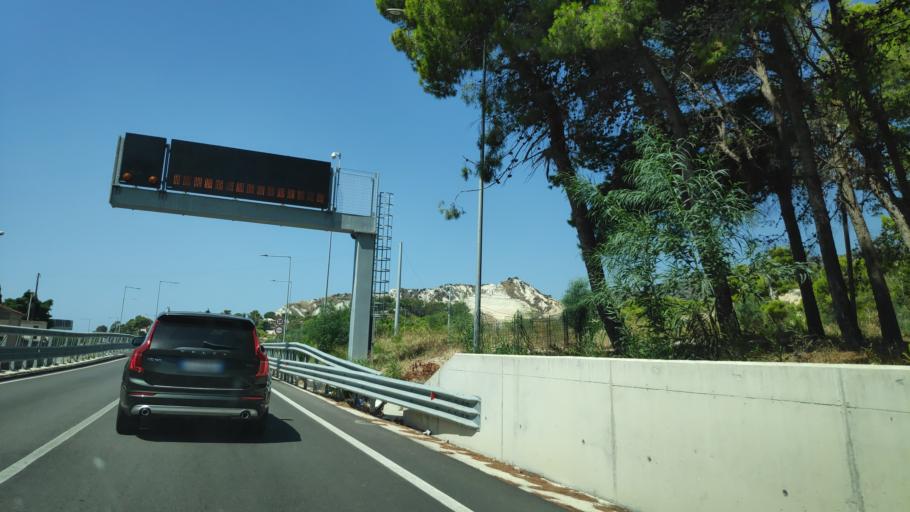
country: IT
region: Calabria
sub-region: Provincia di Reggio Calabria
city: Palizzi Marina
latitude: 37.9221
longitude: 16.0145
